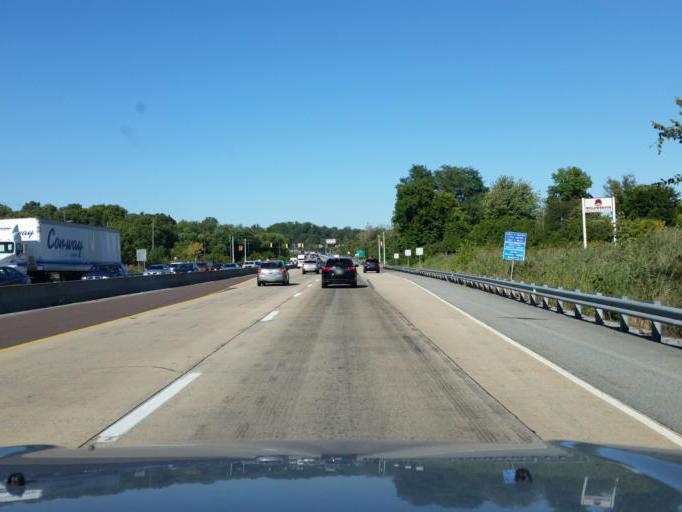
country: US
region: Pennsylvania
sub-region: Chester County
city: West Chester
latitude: 39.9442
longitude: -75.5868
